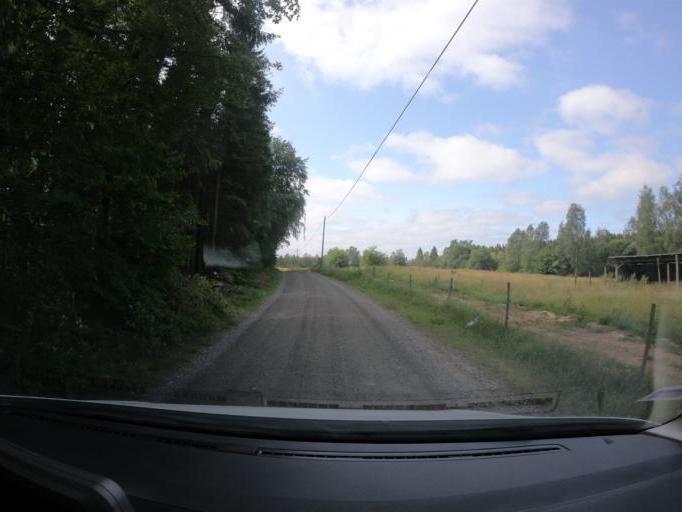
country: SE
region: Skane
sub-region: Hassleholms Kommun
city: Sosdala
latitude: 56.1065
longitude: 13.6479
